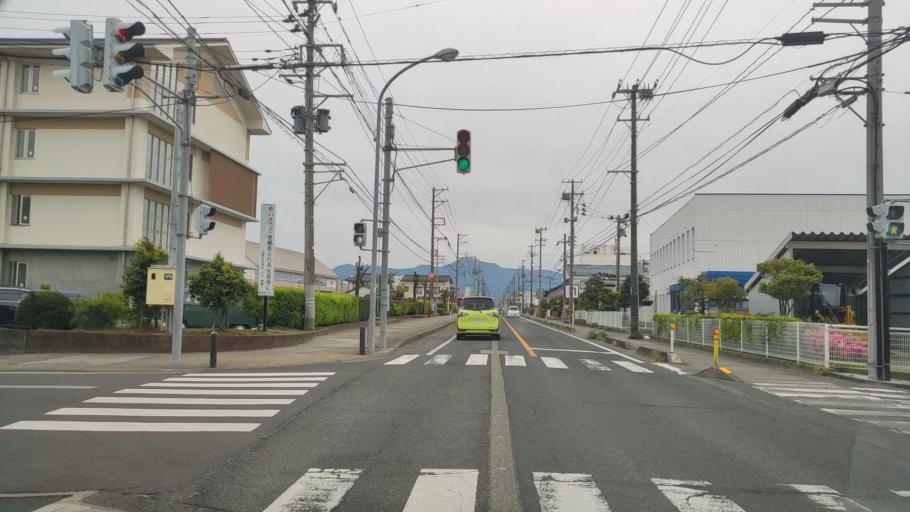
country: JP
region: Niigata
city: Gosen
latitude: 37.7335
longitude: 139.1767
